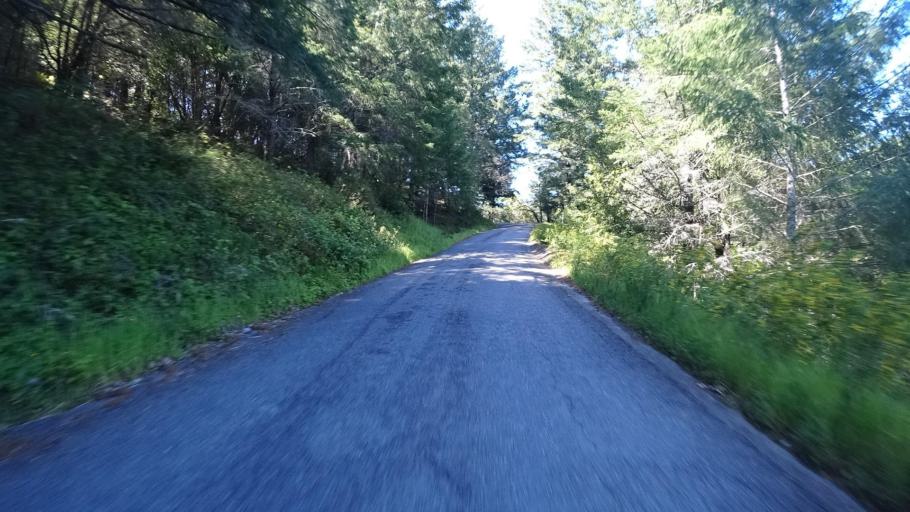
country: US
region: California
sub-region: Humboldt County
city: Rio Dell
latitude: 40.2186
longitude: -124.1116
